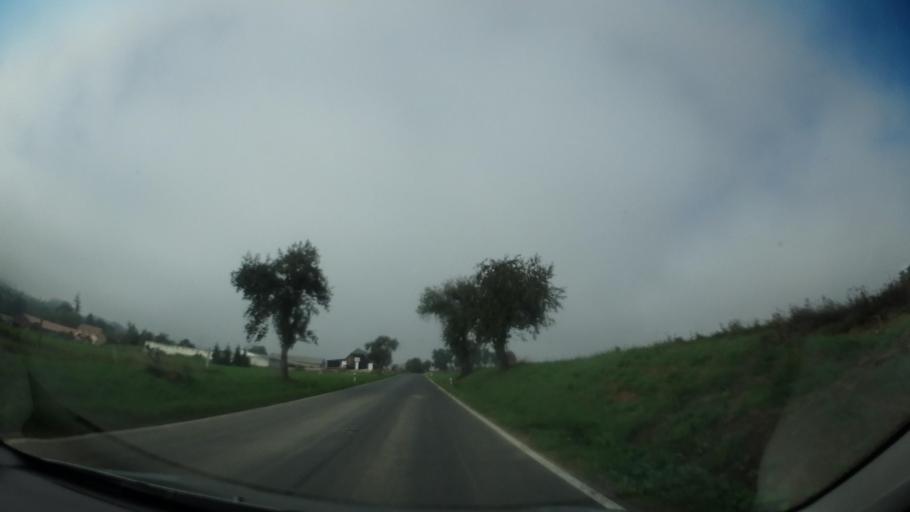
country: CZ
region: Jihocesky
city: Katovice
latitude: 49.2596
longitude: 13.7708
